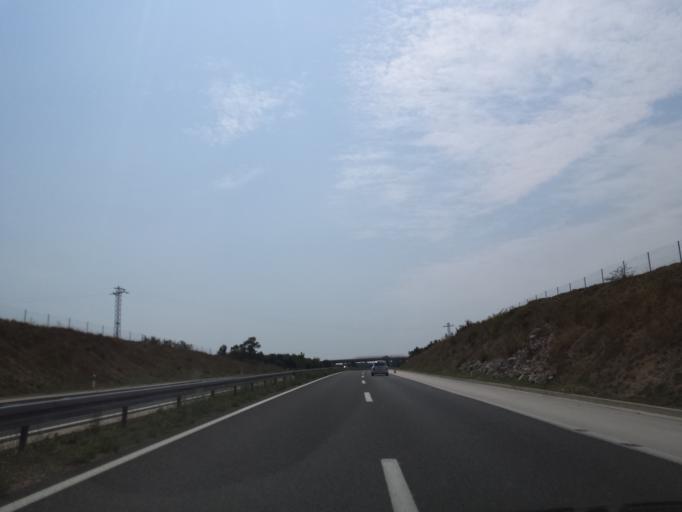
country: HR
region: Zadarska
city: Posedarje
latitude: 44.2053
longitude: 15.4445
